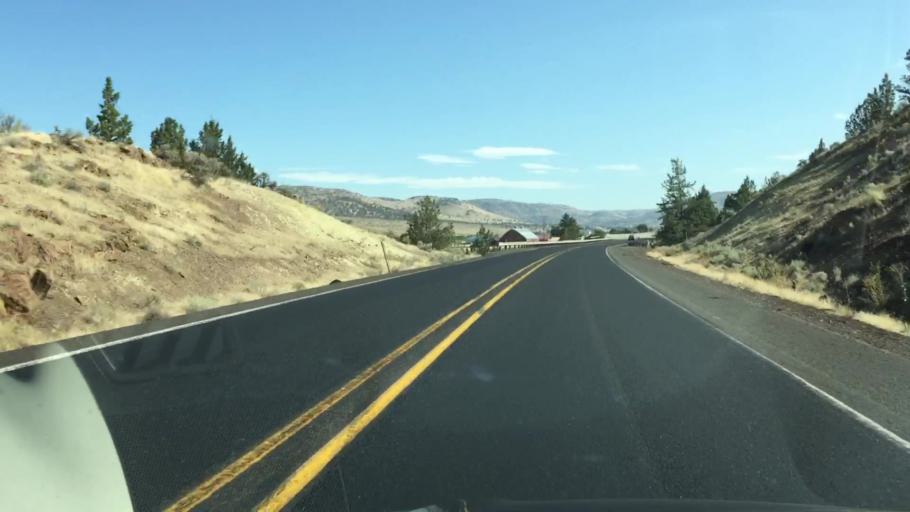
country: US
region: Oregon
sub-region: Jefferson County
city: Madras
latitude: 44.7812
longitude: -120.9659
